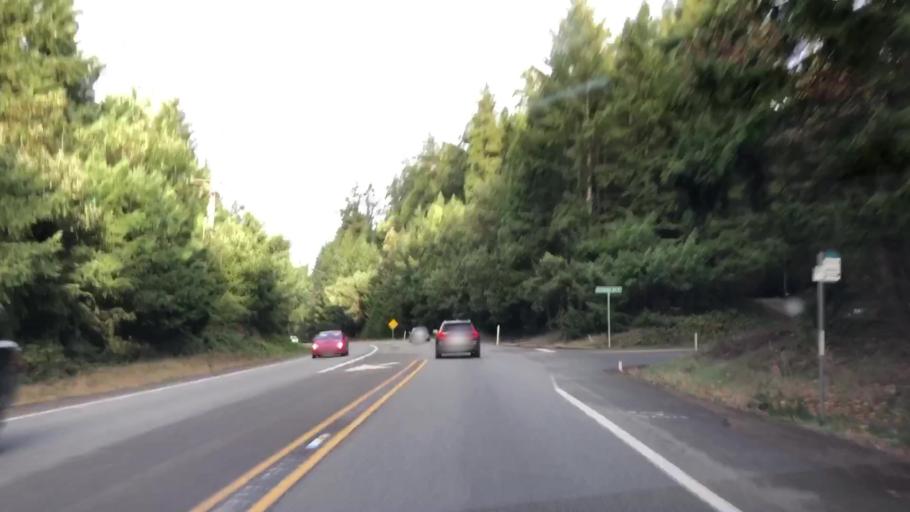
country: US
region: Washington
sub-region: Kitsap County
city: Suquamish
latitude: 47.7033
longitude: -122.5585
